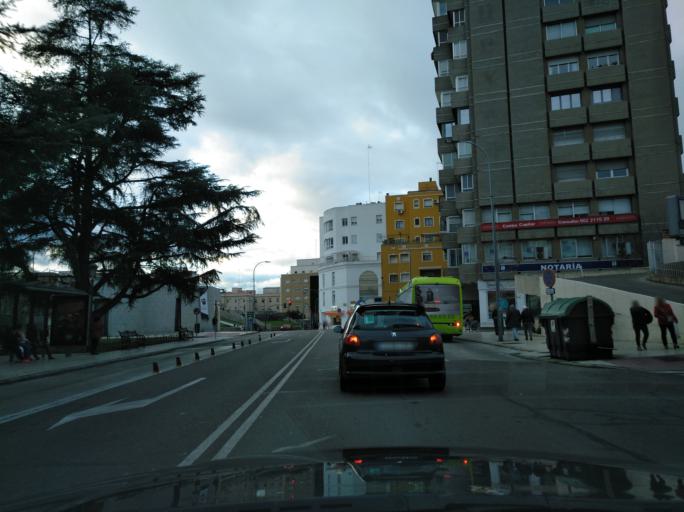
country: ES
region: Extremadura
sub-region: Provincia de Badajoz
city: Badajoz
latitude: 38.8754
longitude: -6.9742
